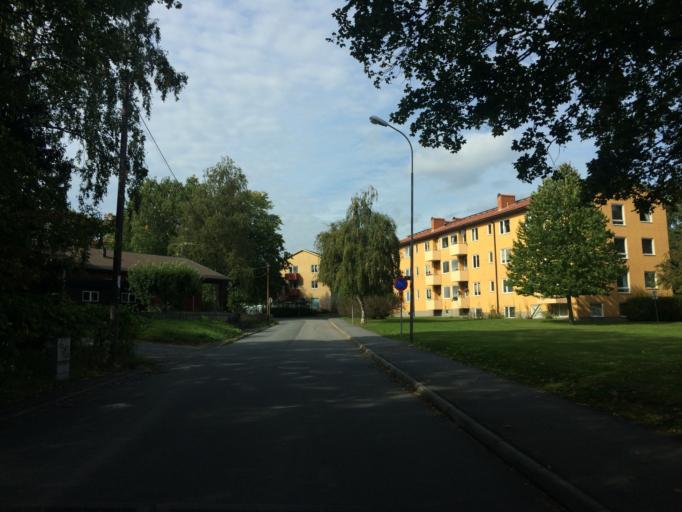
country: SE
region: Stockholm
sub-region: Sollentuna Kommun
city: Sollentuna
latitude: 59.4404
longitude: 17.9401
